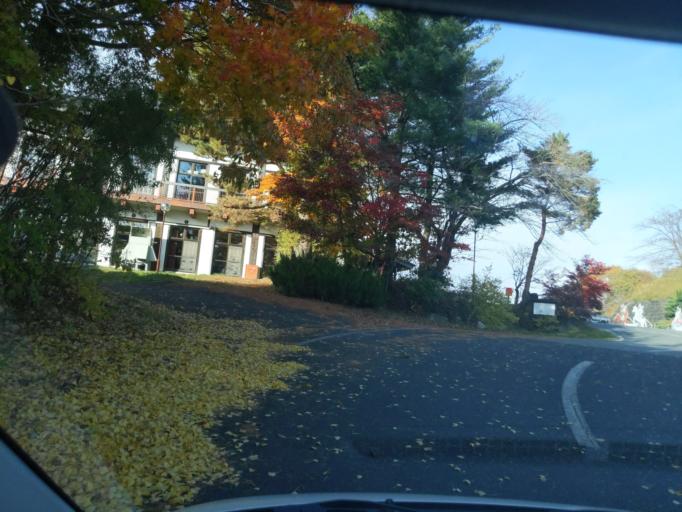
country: JP
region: Iwate
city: Ichinoseki
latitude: 39.0181
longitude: 141.1092
